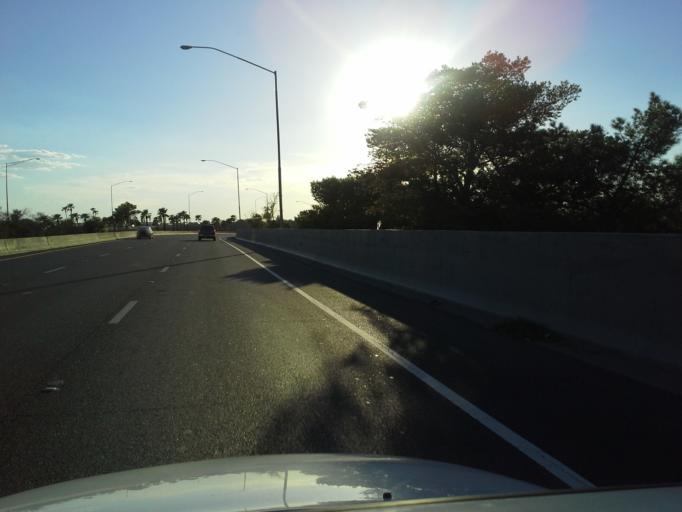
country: US
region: Arizona
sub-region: Maricopa County
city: Phoenix
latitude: 33.4290
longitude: -112.1006
